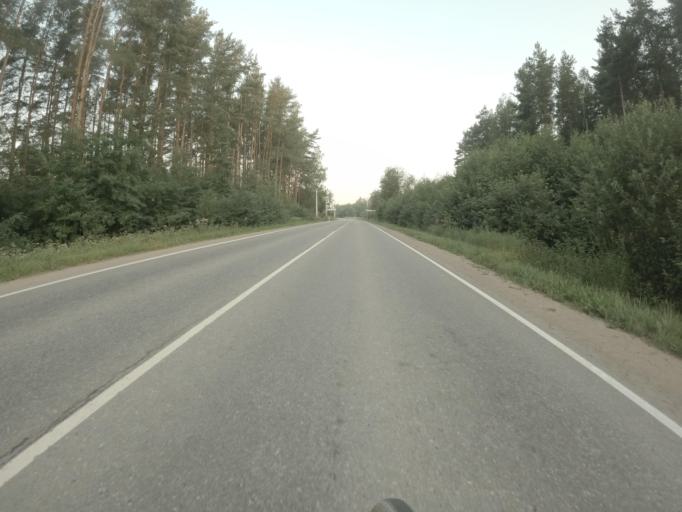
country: RU
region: Leningrad
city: Imeni Sverdlova
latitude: 59.7879
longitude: 30.7217
